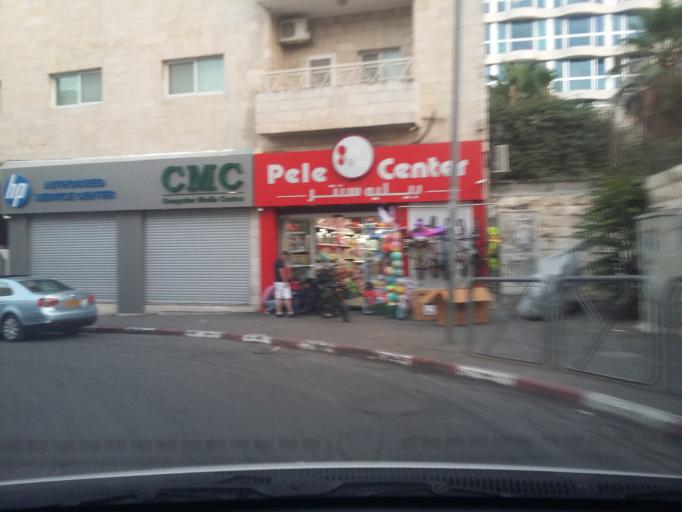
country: PS
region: West Bank
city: East Jerusalem
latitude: 31.7857
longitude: 35.2321
